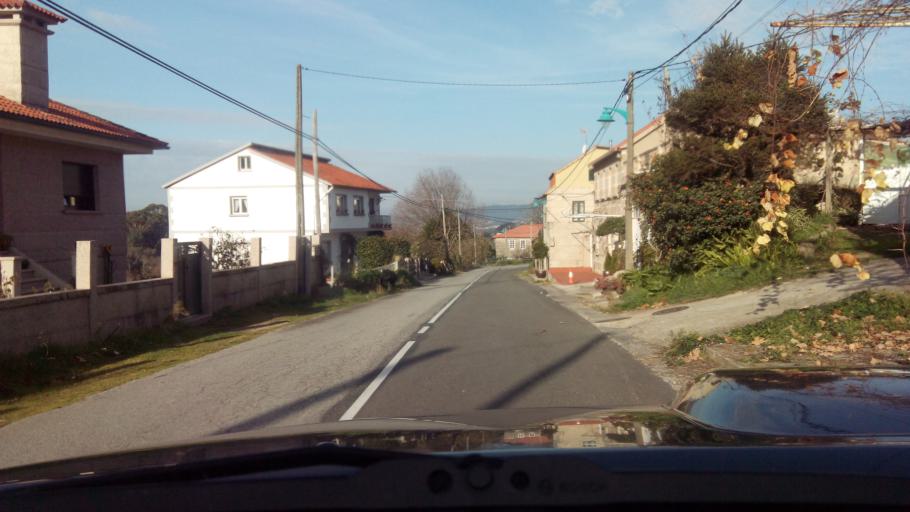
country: ES
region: Galicia
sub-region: Provincia de Pontevedra
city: Marin
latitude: 42.3635
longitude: -8.7167
